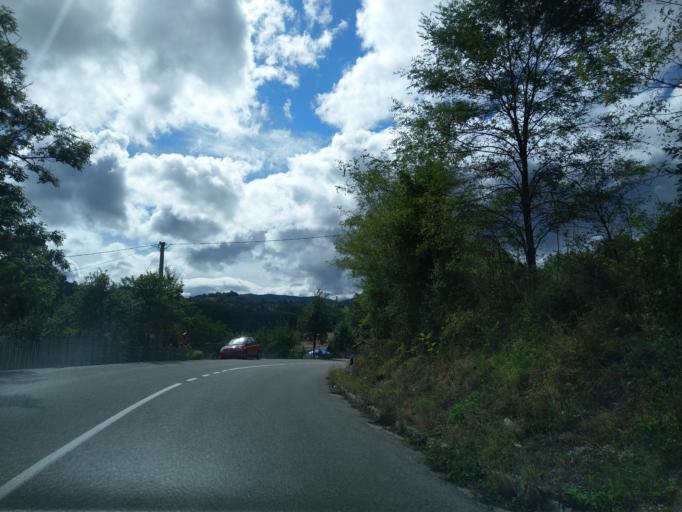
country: RS
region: Central Serbia
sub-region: Zlatiborski Okrug
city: Cajetina
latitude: 43.7200
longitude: 19.7972
